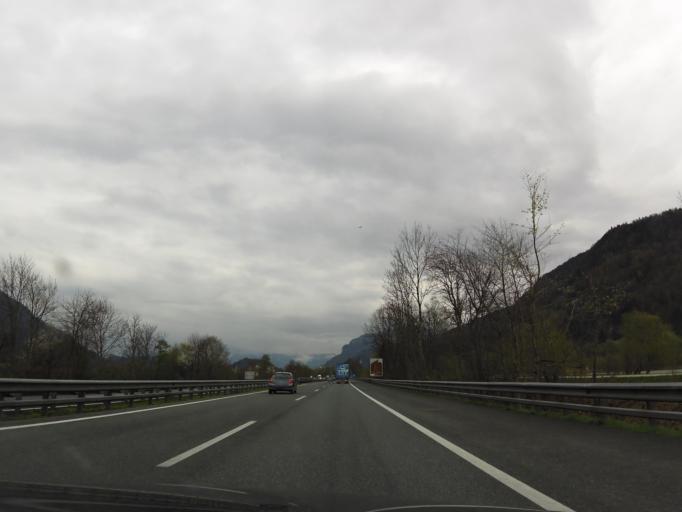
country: AT
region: Tyrol
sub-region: Politischer Bezirk Kufstein
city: Schwoich
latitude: 47.5553
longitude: 12.1272
